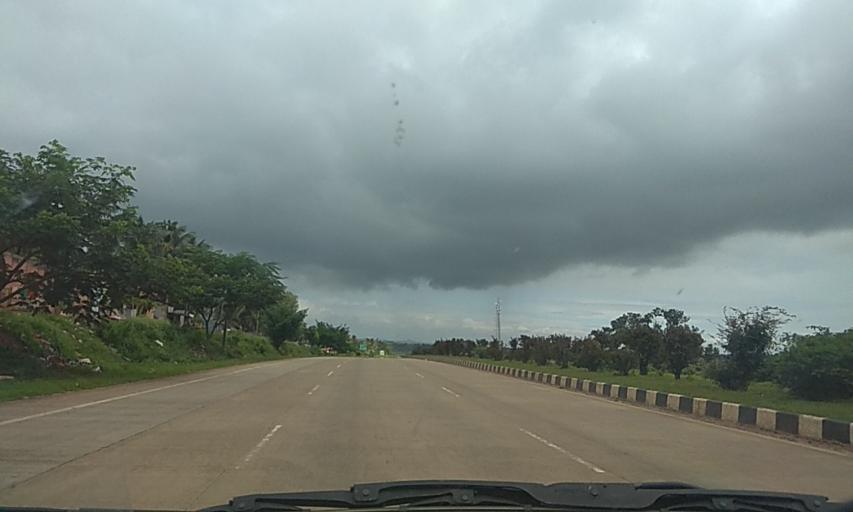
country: IN
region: Karnataka
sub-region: Dharwad
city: Alnavar
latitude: 15.5453
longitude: 74.8671
